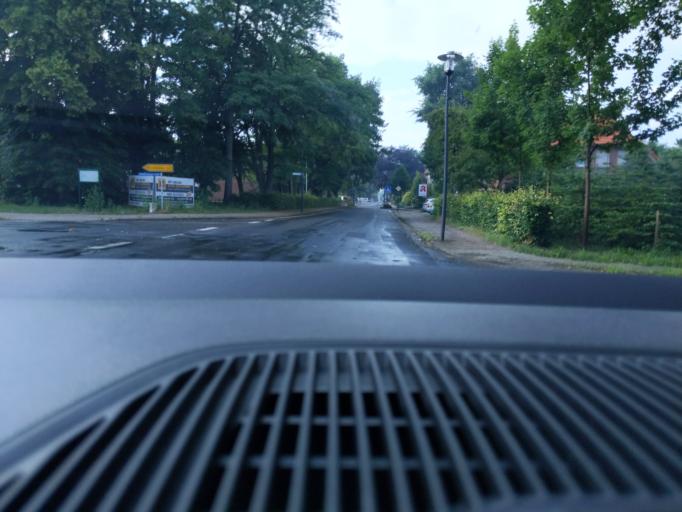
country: NL
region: Drenthe
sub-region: Gemeente Emmen
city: Emmer-Compascuum
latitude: 52.8360
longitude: 7.1012
